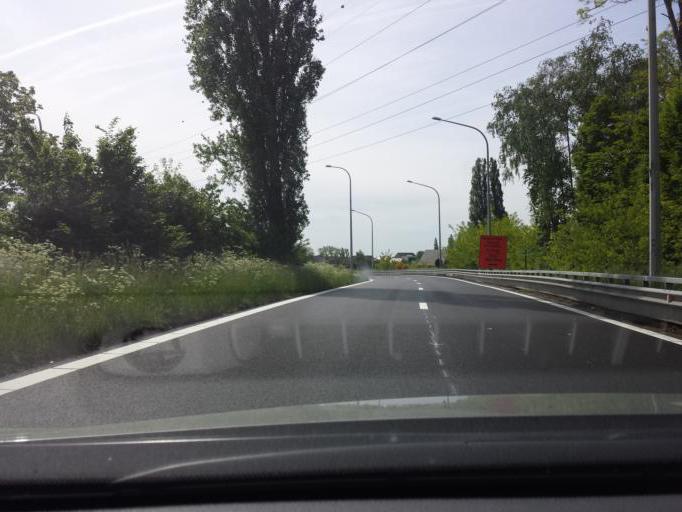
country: BE
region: Flanders
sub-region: Provincie Limburg
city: Hasselt
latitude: 50.9167
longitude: 5.3205
